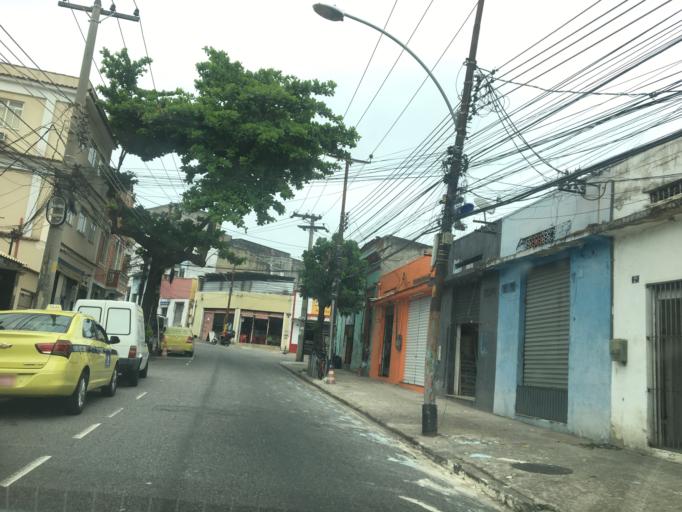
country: BR
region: Rio de Janeiro
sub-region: Rio De Janeiro
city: Rio de Janeiro
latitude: -22.8952
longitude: -43.2287
